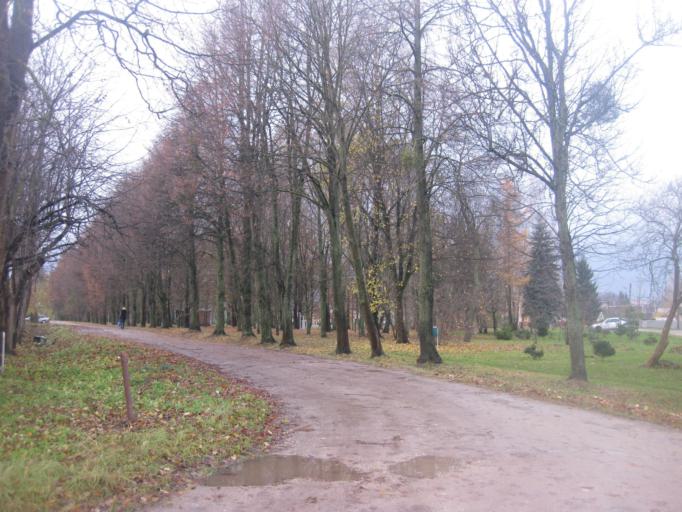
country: LT
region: Kauno apskritis
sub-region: Kaunas
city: Aleksotas
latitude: 54.8578
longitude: 23.8831
